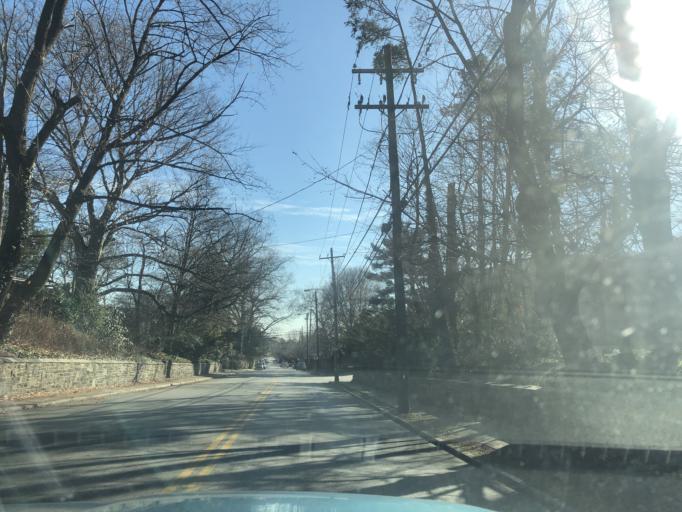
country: US
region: Pennsylvania
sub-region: Montgomery County
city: Bala-Cynwyd
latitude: 40.0003
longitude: -75.2388
